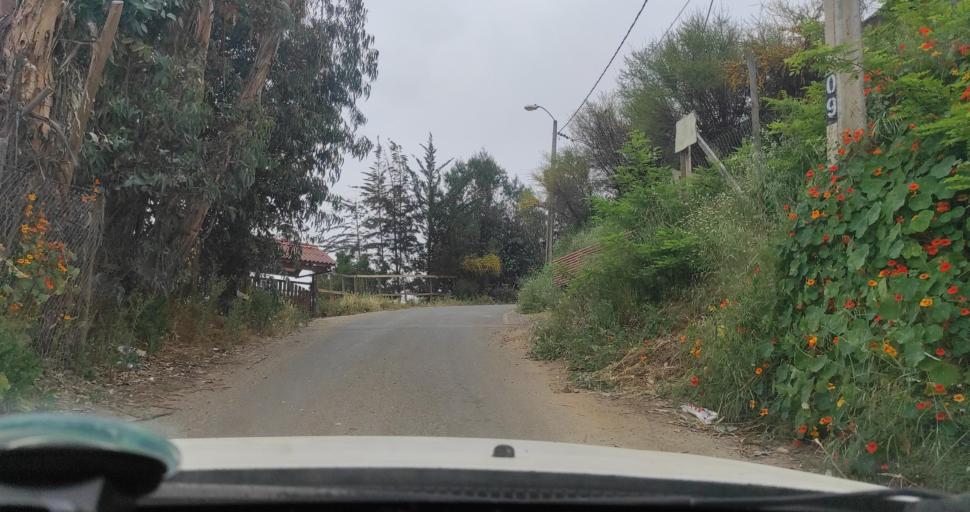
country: CL
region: Valparaiso
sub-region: Provincia de Marga Marga
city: Limache
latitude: -32.9860
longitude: -71.2264
